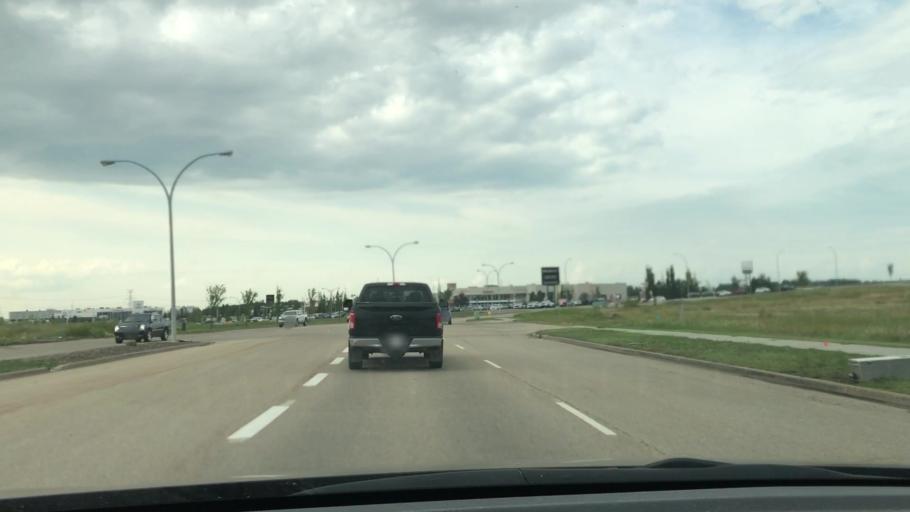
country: CA
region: Alberta
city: Sherwood Park
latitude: 53.5423
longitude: -113.3241
